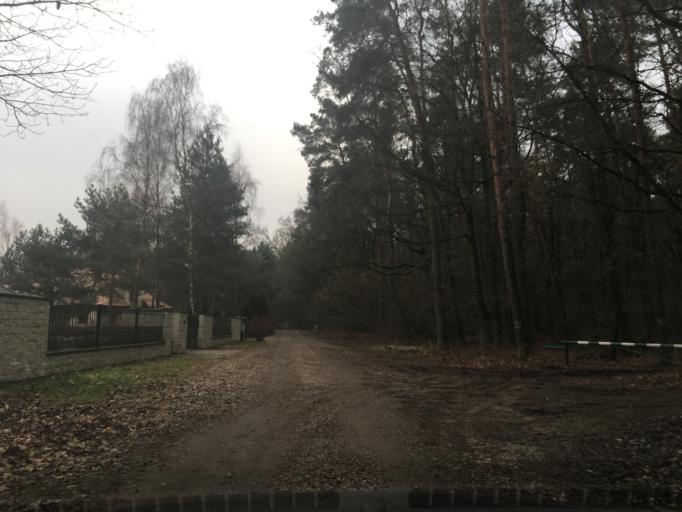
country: PL
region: Masovian Voivodeship
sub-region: Powiat piaseczynski
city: Lesznowola
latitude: 52.0759
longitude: 20.9168
